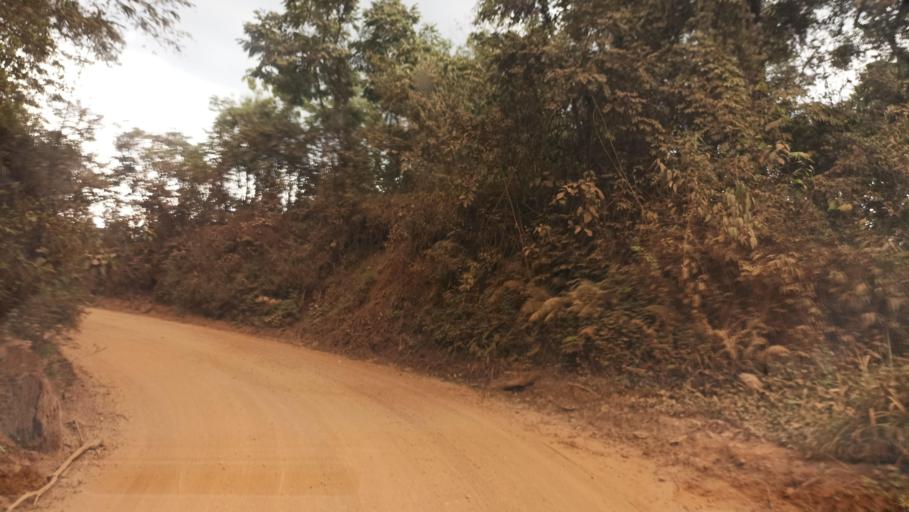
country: BR
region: Minas Gerais
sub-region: Congonhas
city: Congonhas
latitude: -20.4282
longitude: -43.7738
